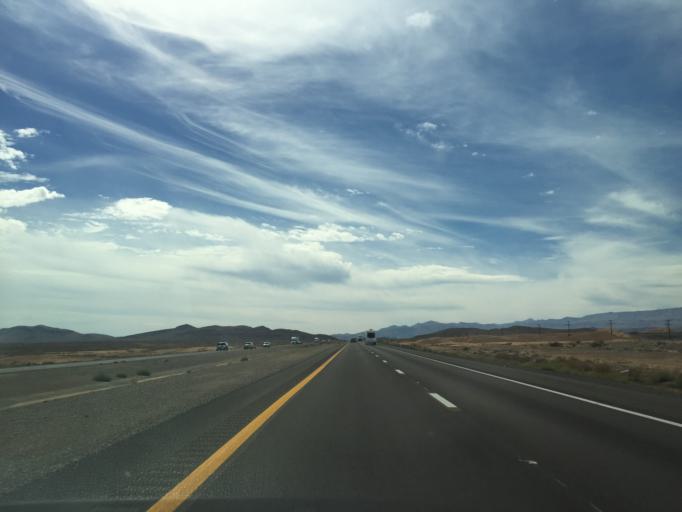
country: US
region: Nevada
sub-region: Clark County
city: Moapa Town
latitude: 36.4906
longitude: -114.7849
